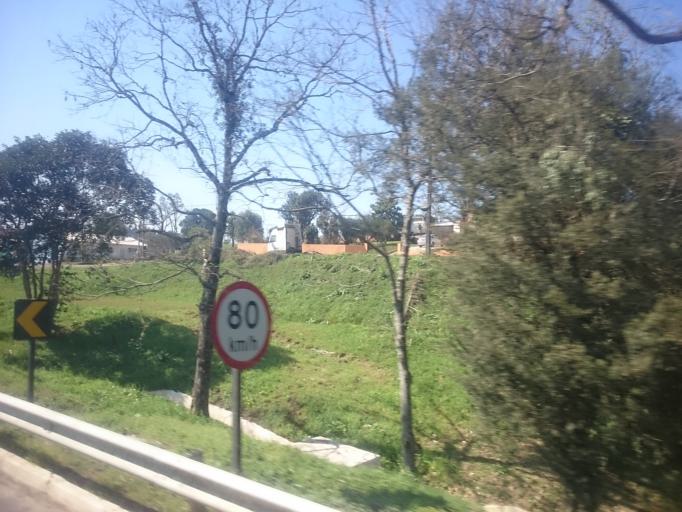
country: BR
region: Santa Catarina
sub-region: Canoinhas
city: Canoinhas
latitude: -26.4571
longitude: -50.2278
